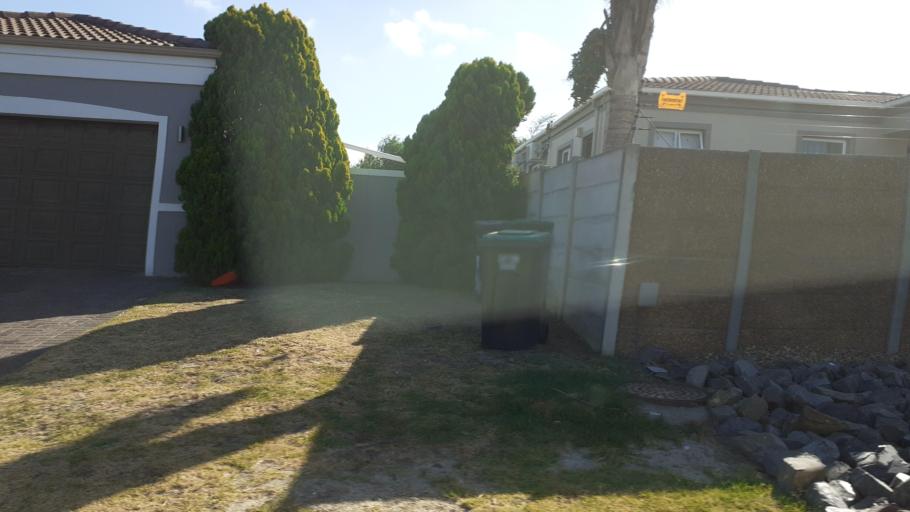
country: ZA
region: Western Cape
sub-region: City of Cape Town
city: Kraaifontein
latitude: -33.8137
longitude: 18.6896
